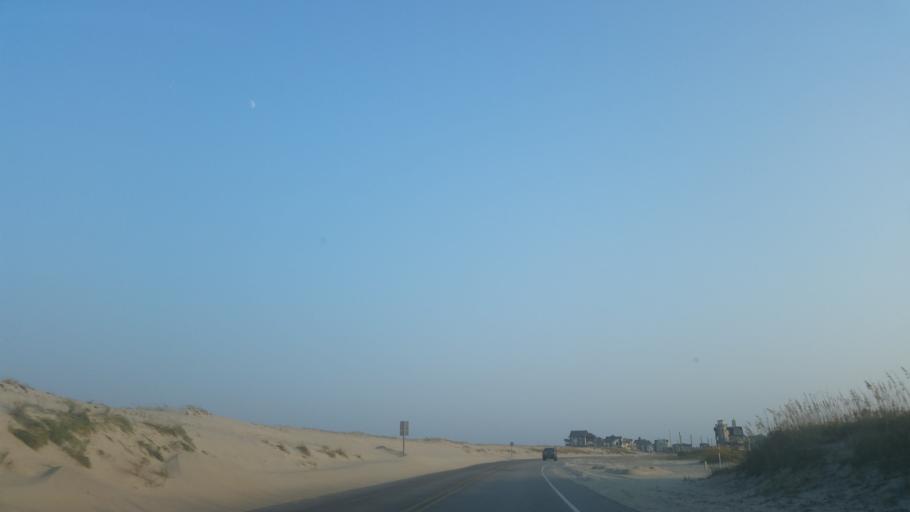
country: US
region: North Carolina
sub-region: Dare County
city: Wanchese
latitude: 35.6104
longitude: -75.4663
